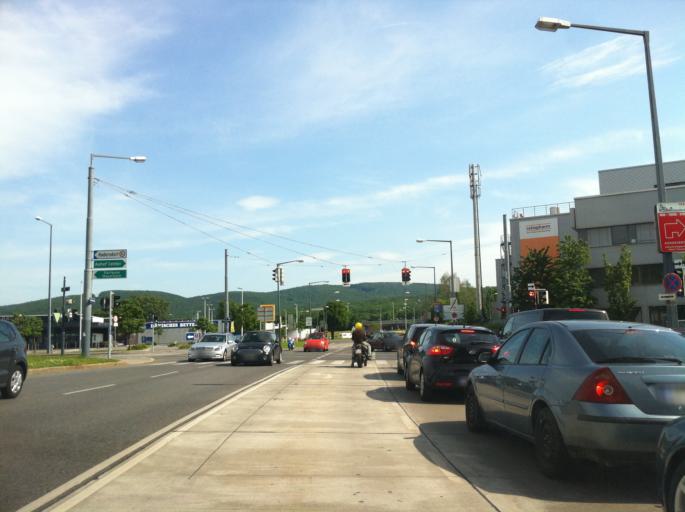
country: AT
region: Lower Austria
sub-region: Politischer Bezirk Wien-Umgebung
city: Purkersdorf
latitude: 48.2076
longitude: 16.2216
